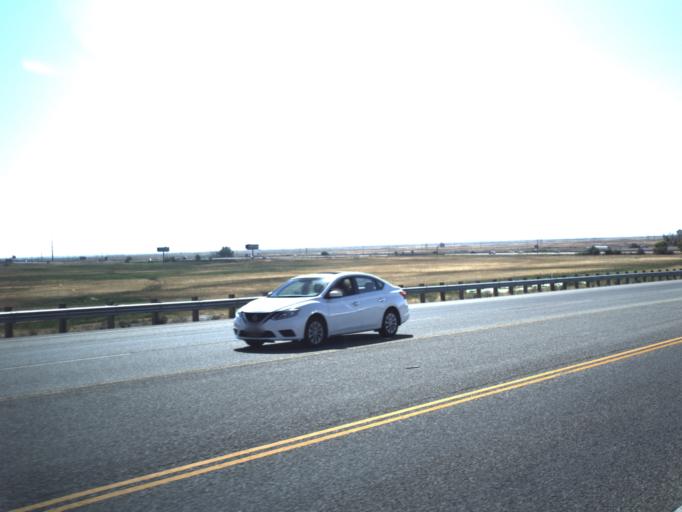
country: US
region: Utah
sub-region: Box Elder County
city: Perry
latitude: 41.4862
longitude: -112.0456
